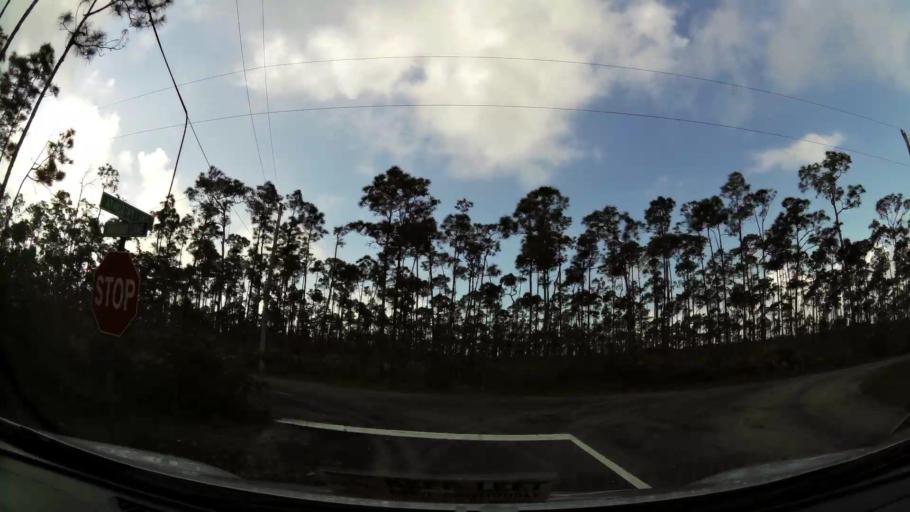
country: BS
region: Freeport
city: Lucaya
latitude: 26.5860
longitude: -78.5504
